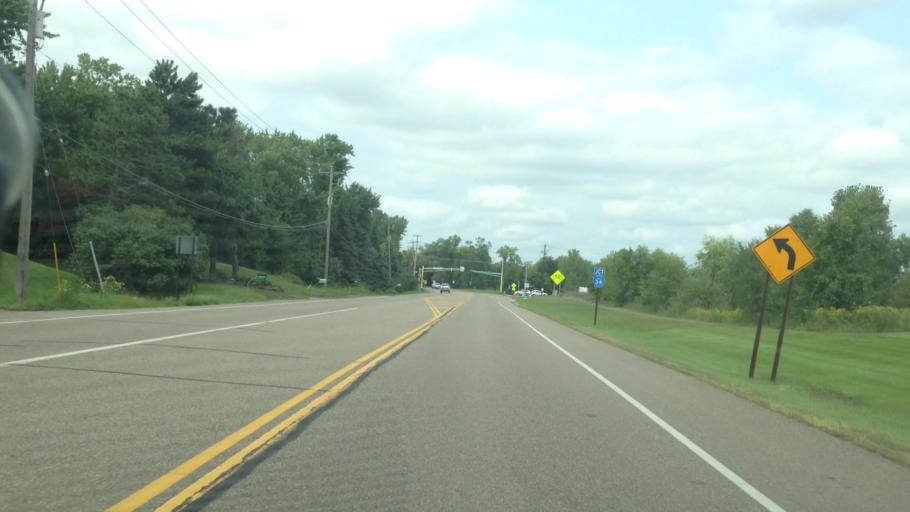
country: US
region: Minnesota
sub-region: Anoka County
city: Circle Pines
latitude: 45.1399
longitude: -93.1267
